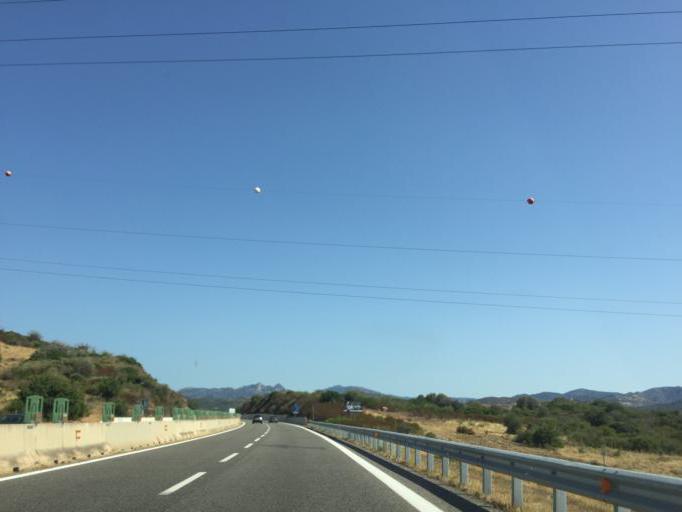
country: IT
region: Sardinia
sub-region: Provincia di Olbia-Tempio
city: Loiri Porto San Paolo
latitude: 40.8761
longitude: 9.5007
